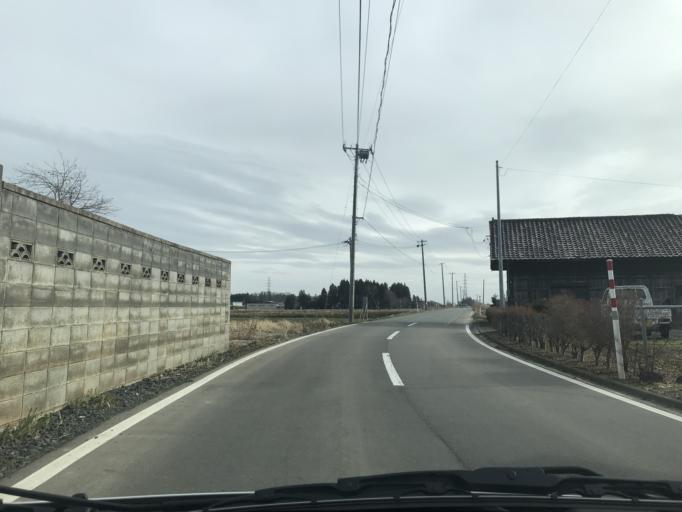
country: JP
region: Iwate
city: Hanamaki
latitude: 39.3449
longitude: 141.0598
